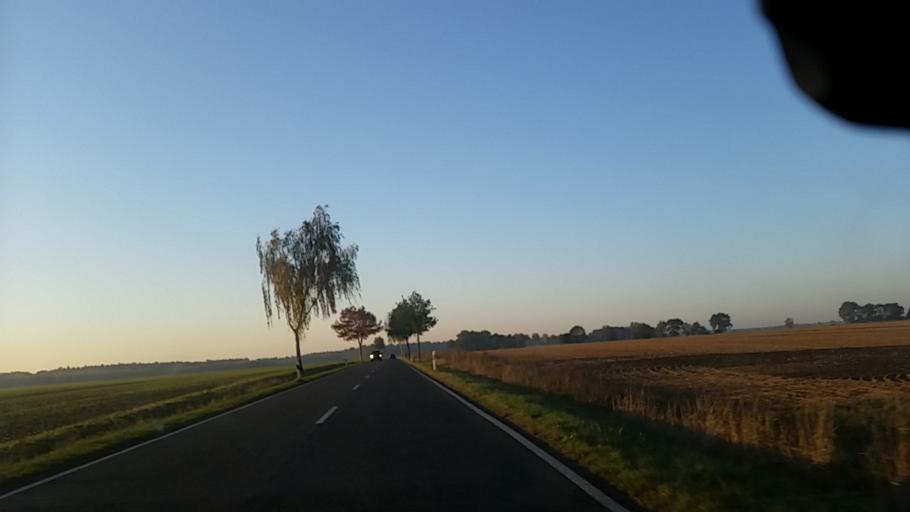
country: DE
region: Lower Saxony
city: Wittingen
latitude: 52.6872
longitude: 10.8070
